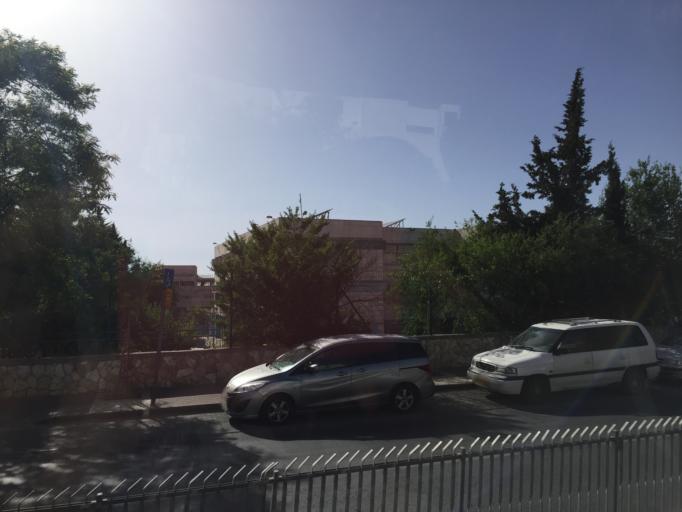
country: IL
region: Jerusalem
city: Jerusalem
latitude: 31.7485
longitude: 35.2182
